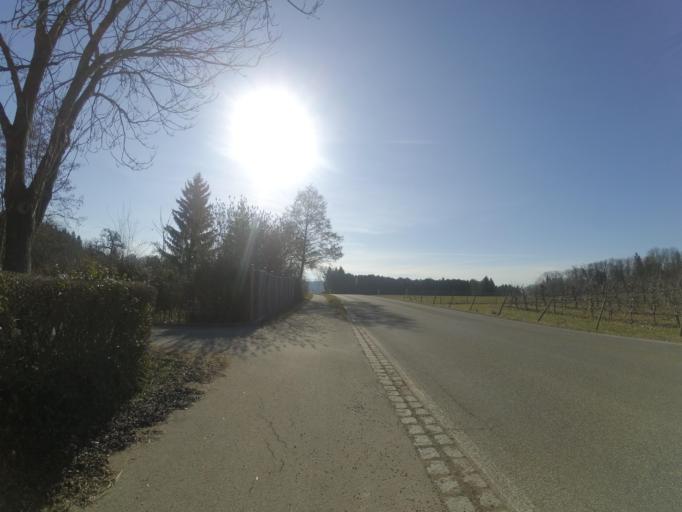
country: DE
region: Baden-Wuerttemberg
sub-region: Tuebingen Region
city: Wolpertswende
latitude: 47.8843
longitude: 9.6189
